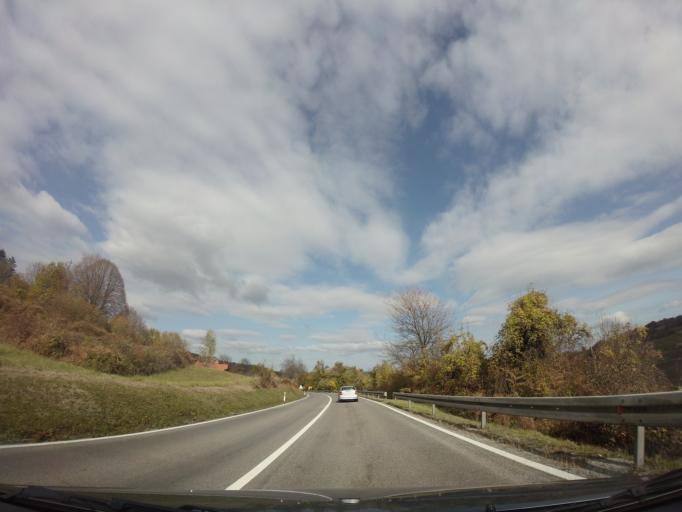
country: HR
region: Karlovacka
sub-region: Grad Karlovac
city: Slunj
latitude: 45.0891
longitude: 15.5943
